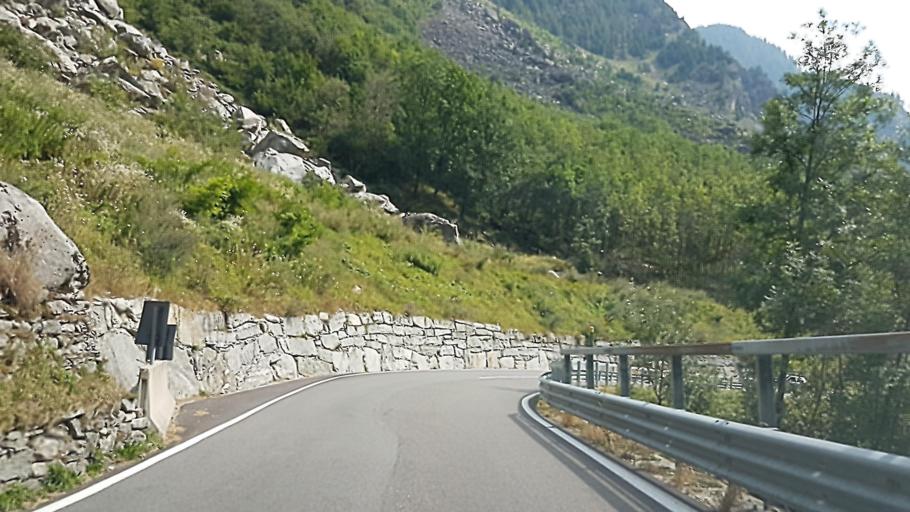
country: IT
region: Lombardy
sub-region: Provincia di Sondrio
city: Campodolcino
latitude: 46.3746
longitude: 9.3603
